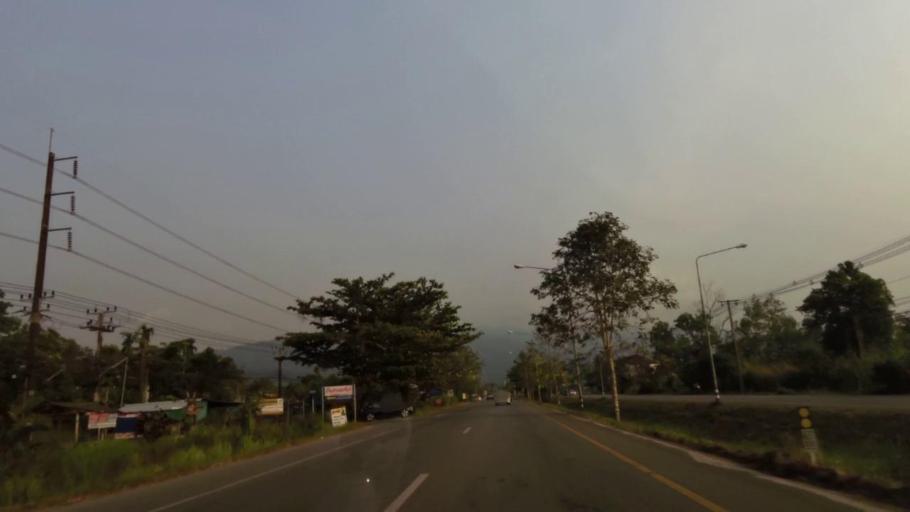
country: TH
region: Chanthaburi
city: Chanthaburi
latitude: 12.5939
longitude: 102.1466
